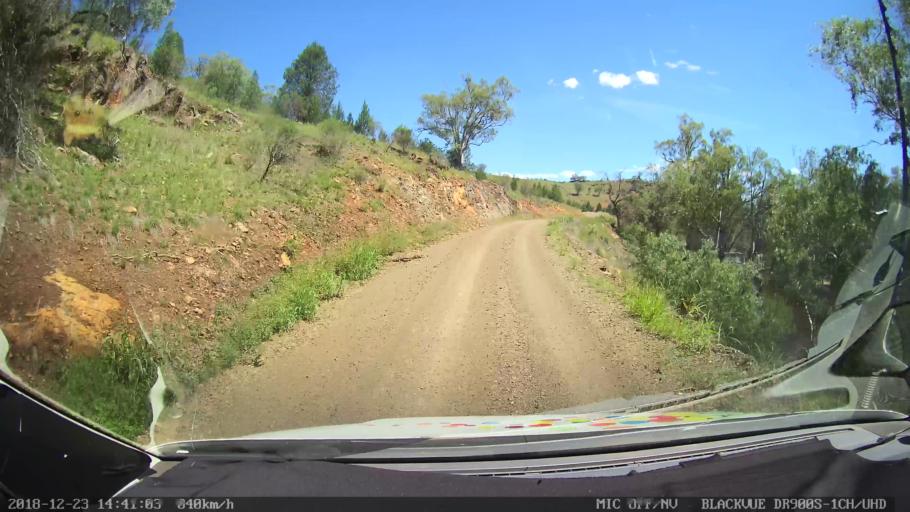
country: AU
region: New South Wales
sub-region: Tamworth Municipality
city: Manilla
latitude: -30.6294
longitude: 150.9027
